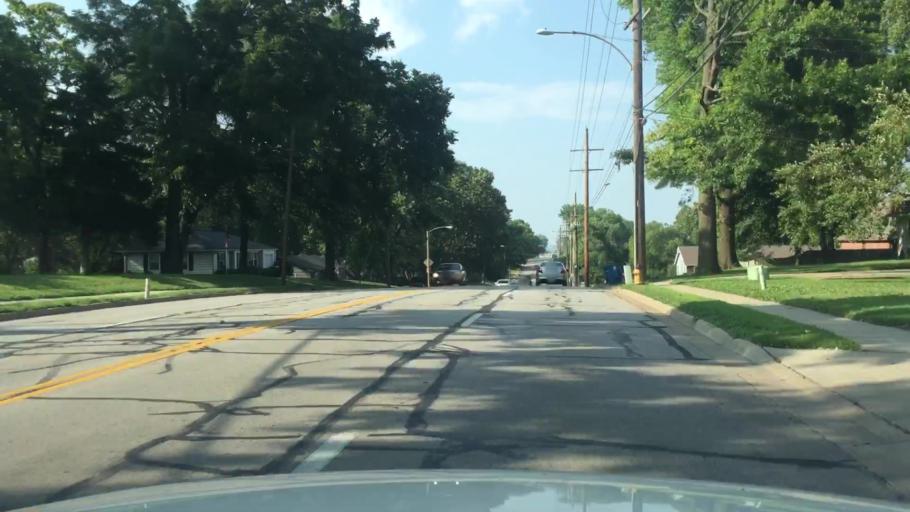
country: US
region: Kansas
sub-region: Johnson County
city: Shawnee
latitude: 39.0321
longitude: -94.7145
